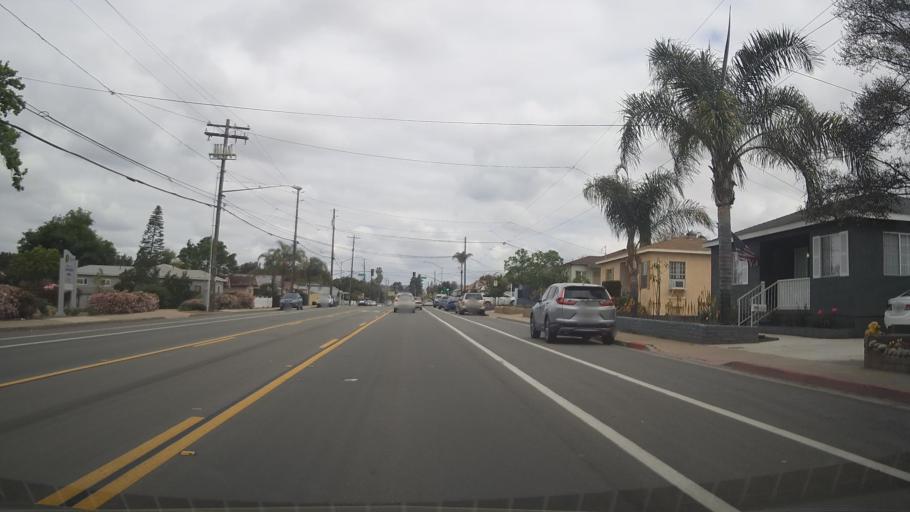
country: US
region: California
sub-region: San Diego County
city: La Mesa
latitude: 32.7618
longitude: -117.0468
